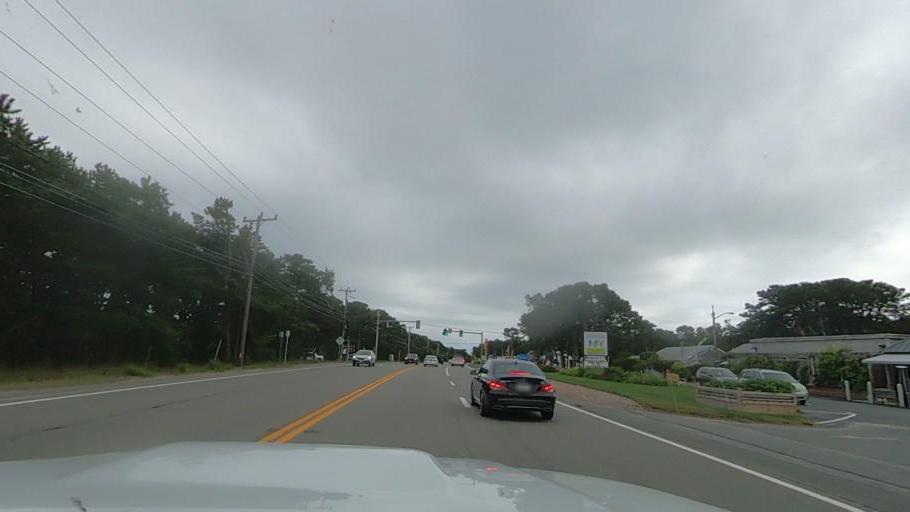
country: US
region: Massachusetts
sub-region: Barnstable County
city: North Eastham
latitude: 41.9054
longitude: -69.9850
